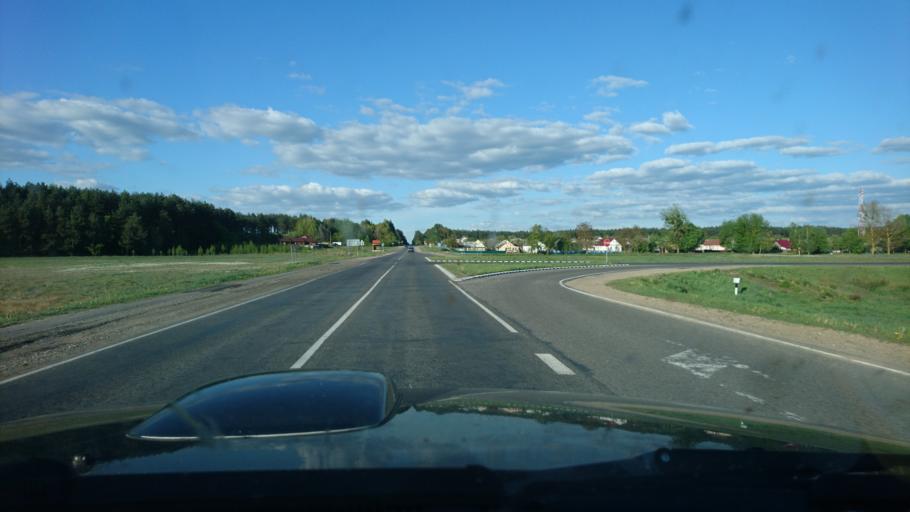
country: BY
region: Brest
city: Ivatsevichy
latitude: 52.7240
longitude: 25.3678
